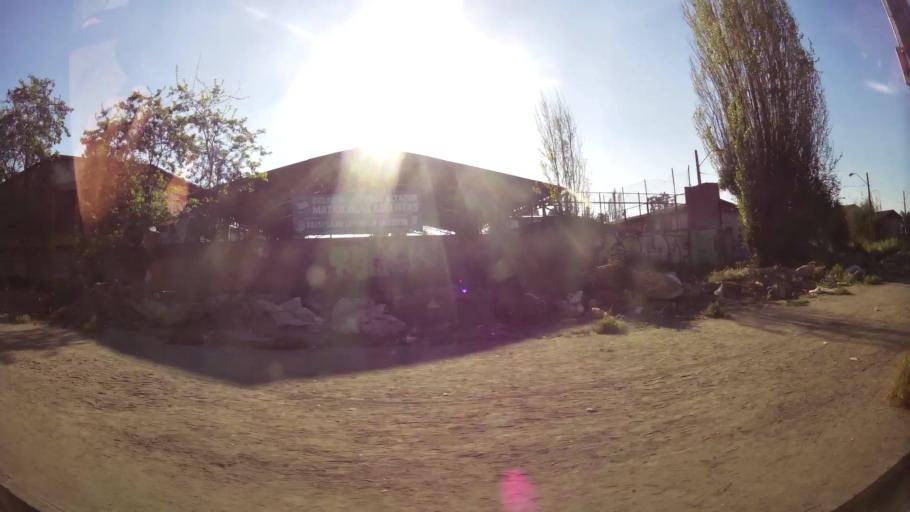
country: CL
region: Santiago Metropolitan
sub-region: Provincia de Talagante
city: Penaflor
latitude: -33.6051
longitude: -70.8668
